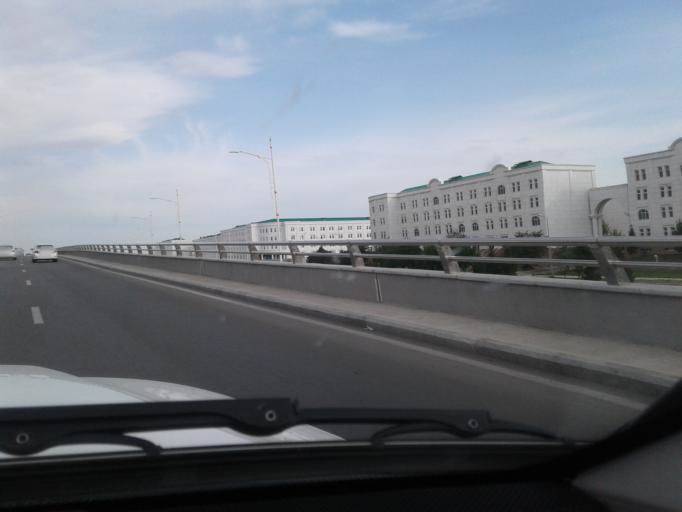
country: TM
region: Ahal
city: Ashgabat
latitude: 37.9791
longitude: 58.3400
